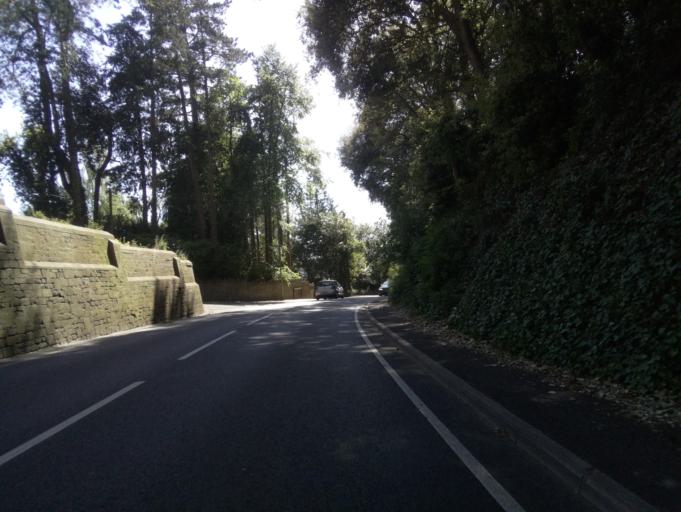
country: GB
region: England
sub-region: Somerset
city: Crewkerne
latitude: 50.8866
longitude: -2.7855
